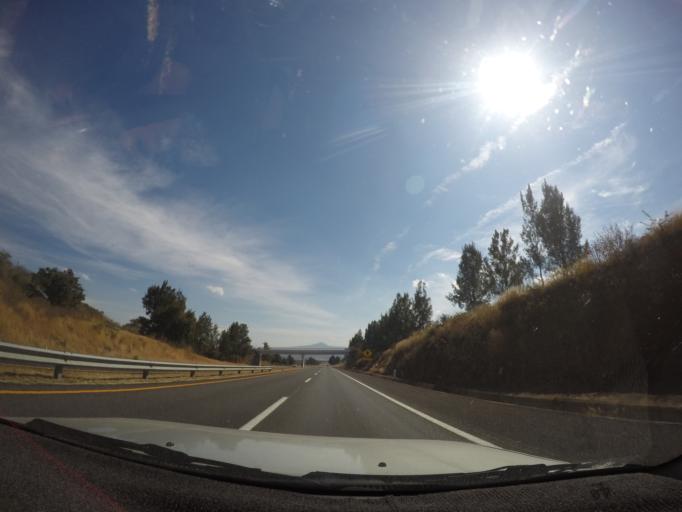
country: MX
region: Michoacan
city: Penjamillo de Degollado
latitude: 20.0386
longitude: -101.9328
